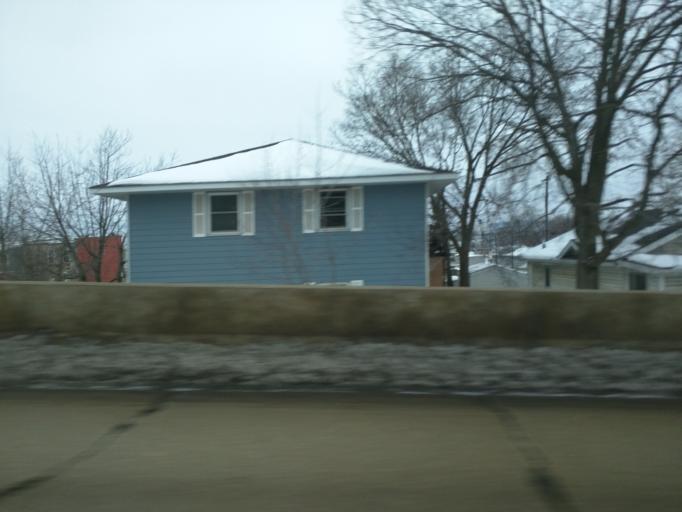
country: US
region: Wisconsin
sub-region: La Crosse County
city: North La Crosse
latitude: 43.8336
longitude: -91.2482
